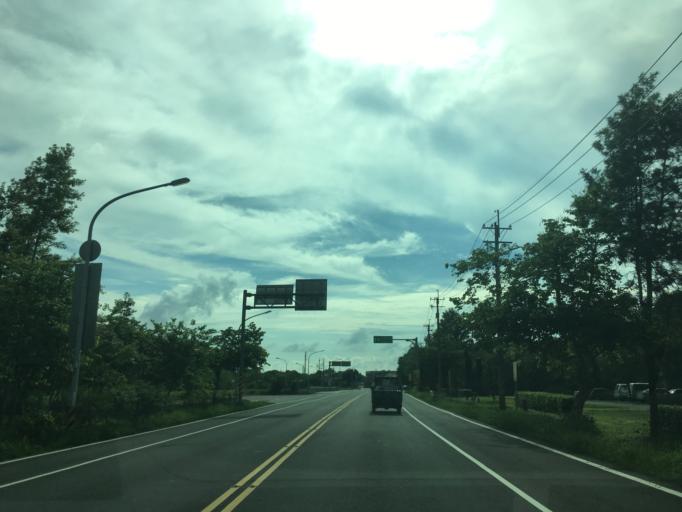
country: TW
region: Taiwan
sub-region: Chiayi
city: Jiayi Shi
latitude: 23.4528
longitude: 120.5600
